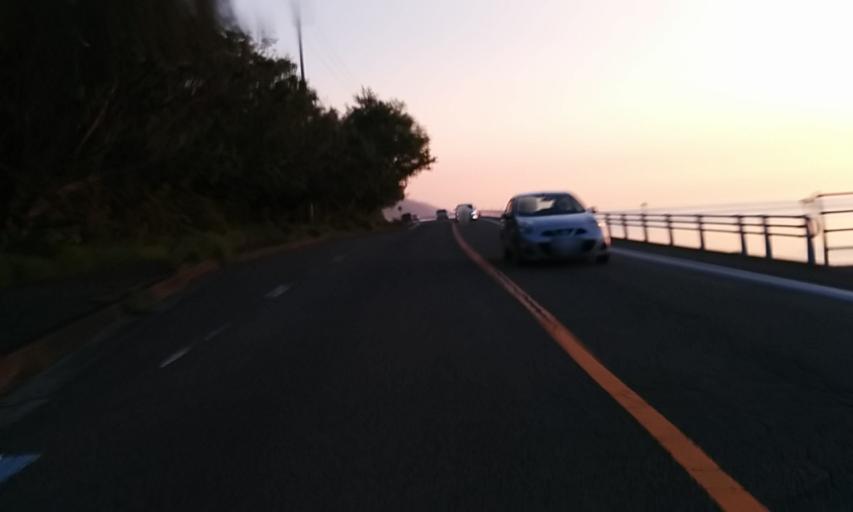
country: JP
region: Ehime
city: Iyo
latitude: 33.6648
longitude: 132.6043
